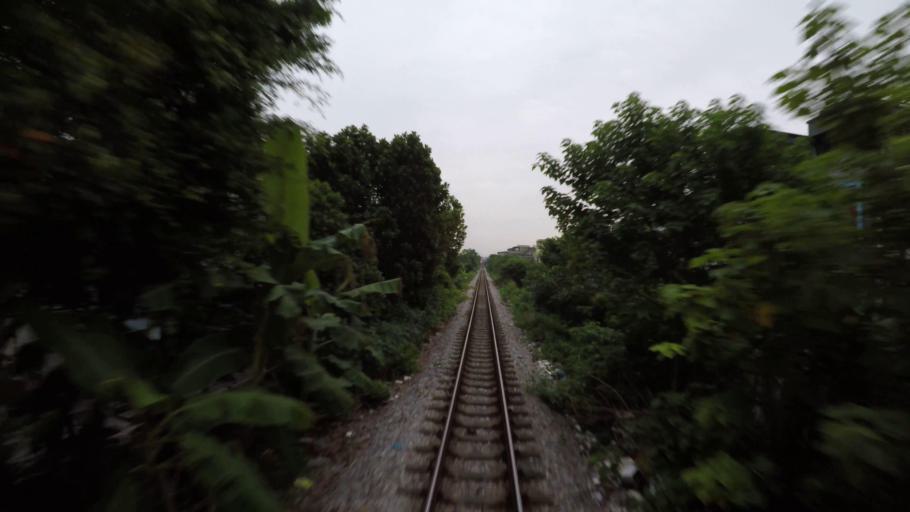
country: VN
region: Ha Noi
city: Hoan Kiem
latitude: 21.0464
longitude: 105.8939
